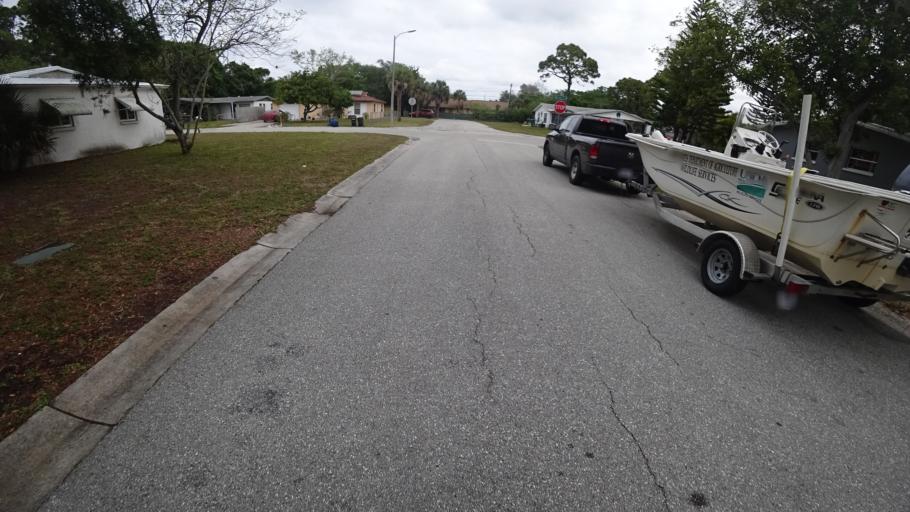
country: US
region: Florida
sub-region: Manatee County
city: South Bradenton
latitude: 27.4580
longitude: -82.5830
